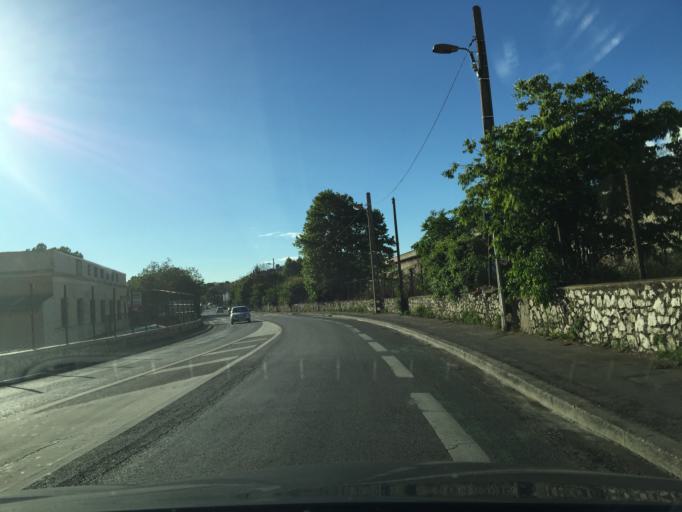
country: FR
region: Provence-Alpes-Cote d'Azur
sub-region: Departement des Bouches-du-Rhone
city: Marseille 11
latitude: 43.2909
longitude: 5.4625
